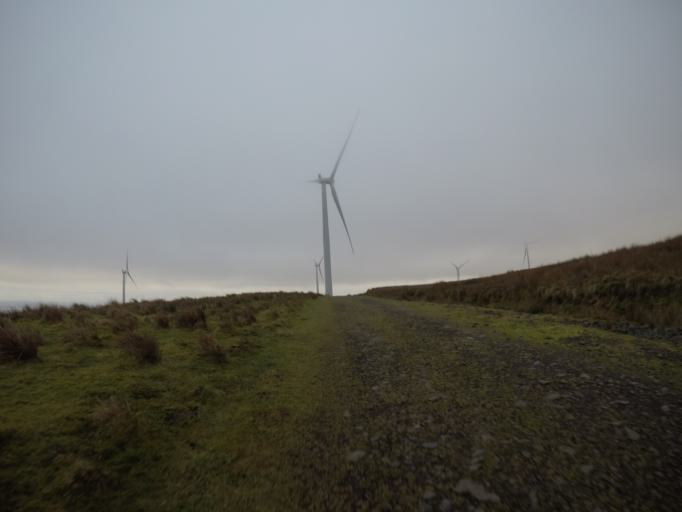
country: GB
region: Scotland
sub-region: North Ayrshire
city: Dalry
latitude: 55.7379
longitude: -4.7777
